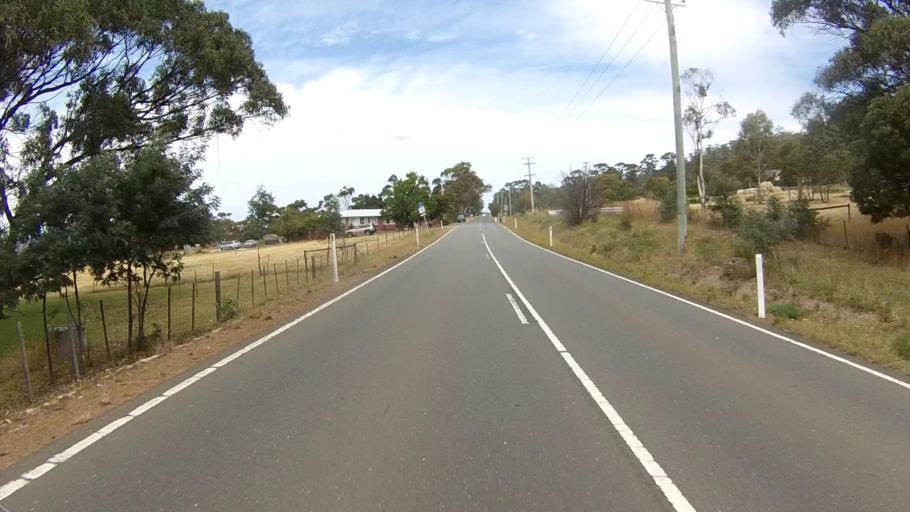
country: AU
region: Tasmania
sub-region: Clarence
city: Acton Park
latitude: -42.8937
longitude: 147.4817
